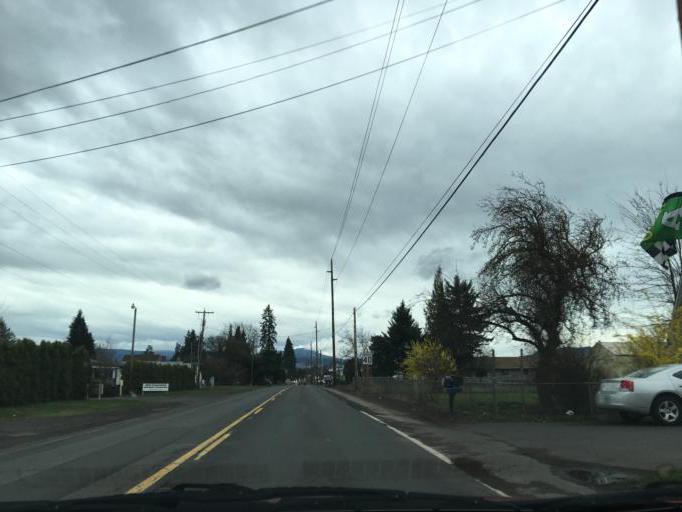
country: US
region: Oregon
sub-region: Hood River County
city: Hood River
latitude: 45.6842
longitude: -121.5289
